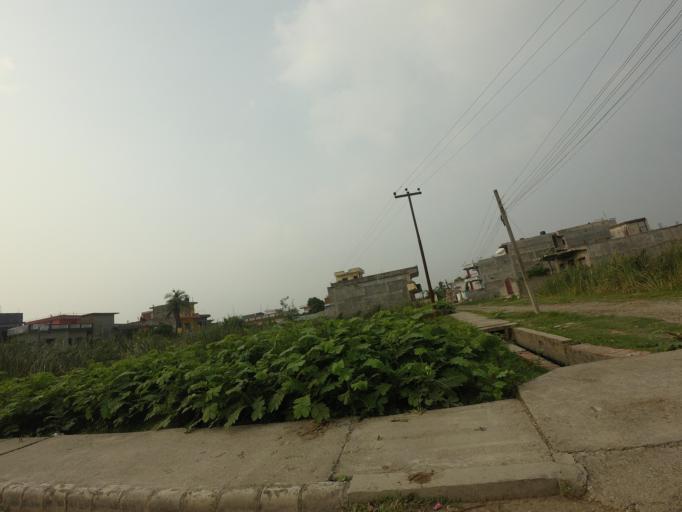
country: NP
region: Western Region
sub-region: Lumbini Zone
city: Bhairahawa
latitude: 27.5049
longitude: 83.4467
